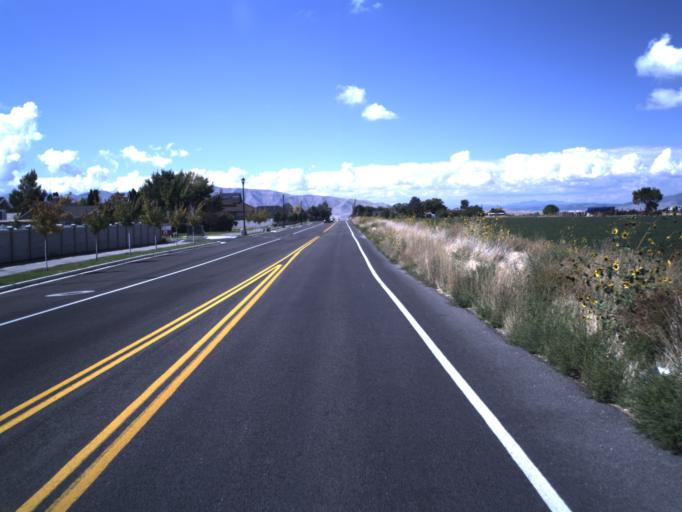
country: US
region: Utah
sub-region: Utah County
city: Spanish Fork
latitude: 40.1154
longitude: -111.6215
